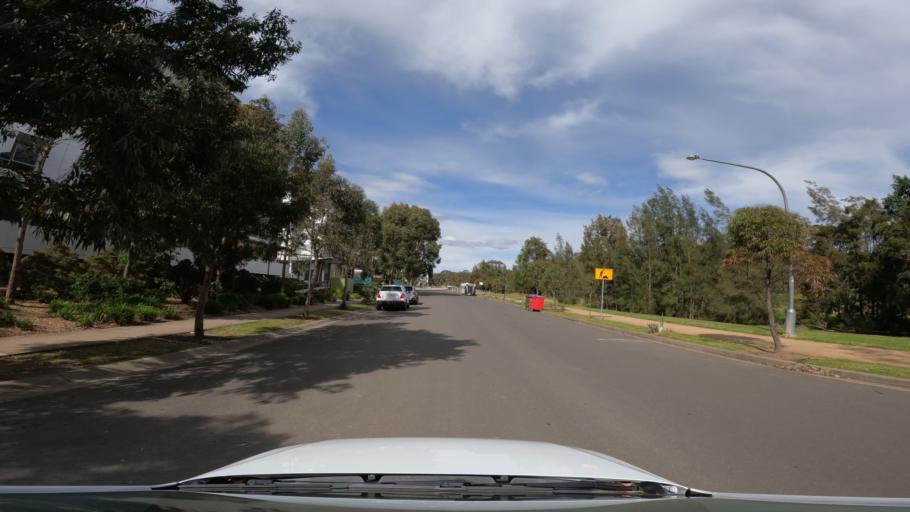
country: AU
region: New South Wales
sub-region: Blacktown
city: Stanhope Gardens
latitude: -33.7207
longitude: 150.9426
